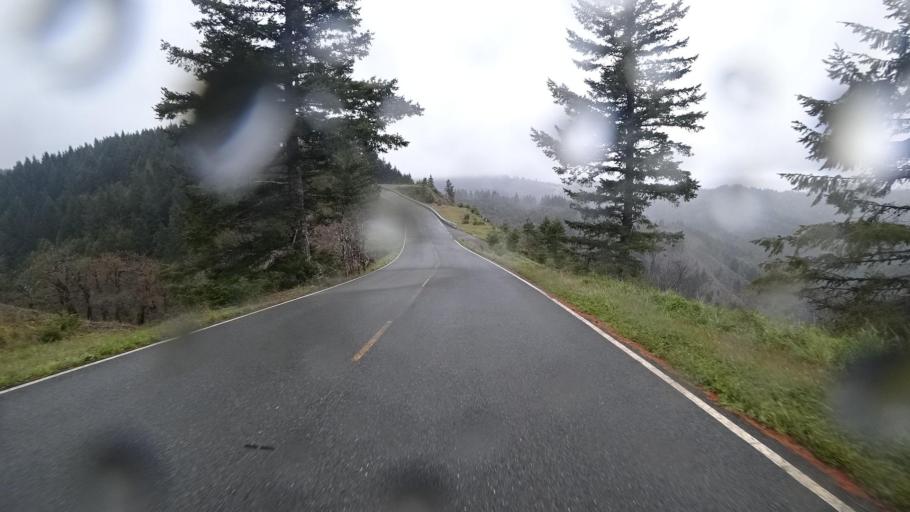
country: US
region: California
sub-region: Humboldt County
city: Westhaven-Moonstone
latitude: 41.1464
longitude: -123.8440
